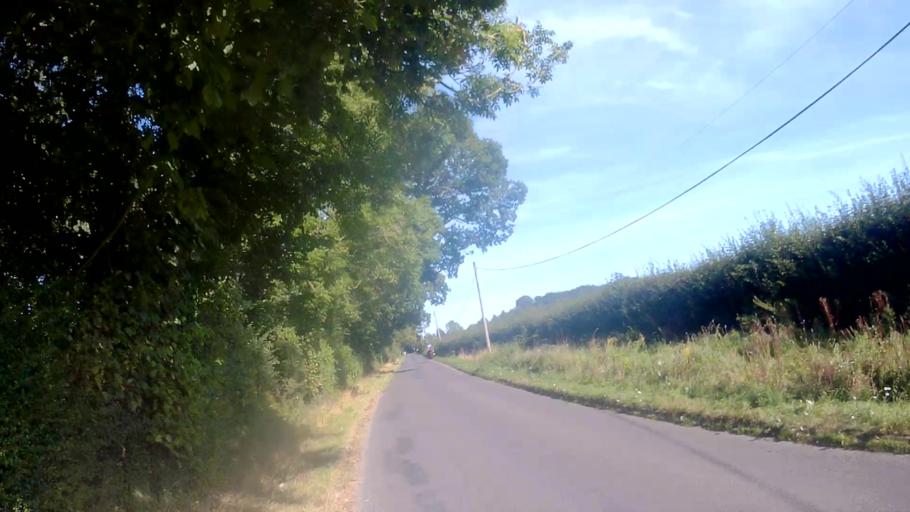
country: GB
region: England
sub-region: Hampshire
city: Overton
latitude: 51.1570
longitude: -1.2324
